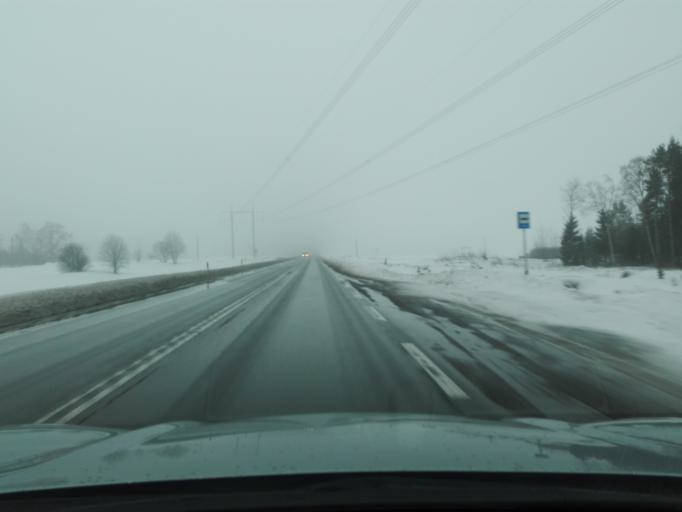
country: EE
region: Raplamaa
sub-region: Kohila vald
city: Kohila
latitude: 59.2137
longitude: 24.7771
